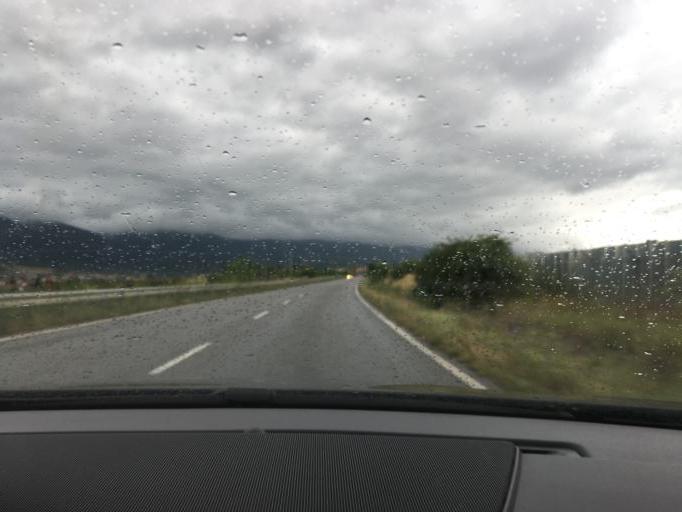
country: BG
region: Kyustendil
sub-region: Obshtina Kyustendil
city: Kyustendil
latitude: 42.2860
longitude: 22.6658
